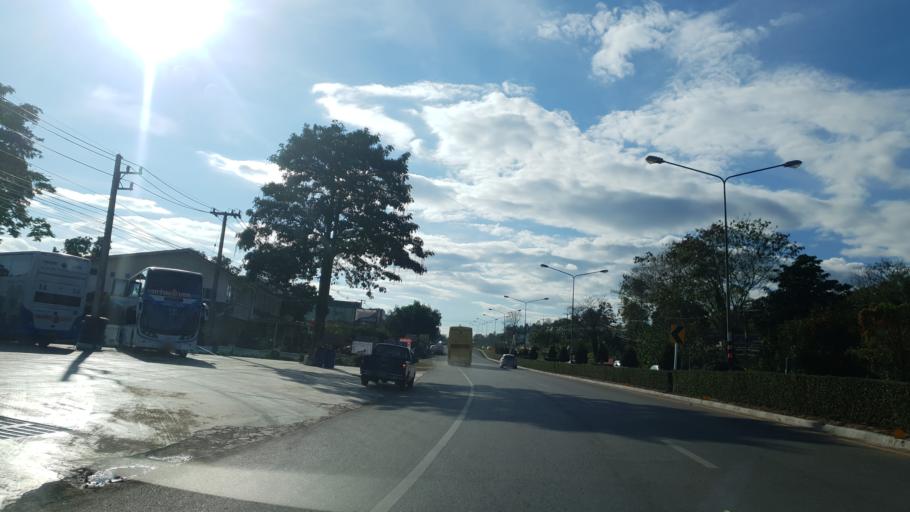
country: TH
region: Loei
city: Phu Ruea
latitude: 17.4574
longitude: 101.3727
